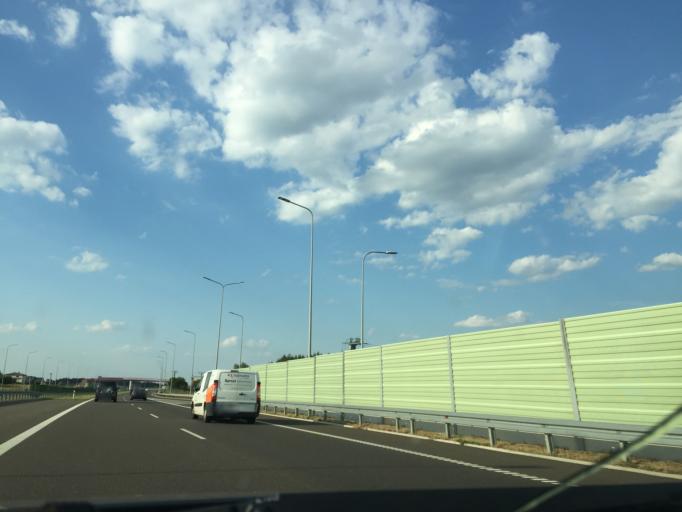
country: PL
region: Masovian Voivodeship
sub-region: Powiat radomski
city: Wolanow
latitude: 51.3863
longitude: 21.0235
